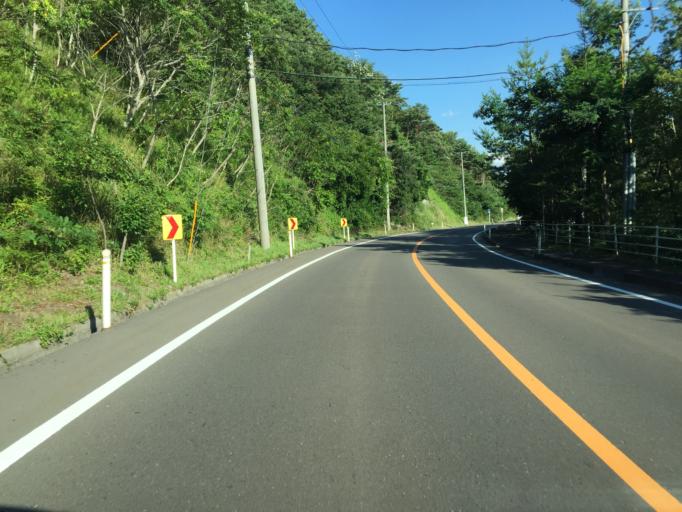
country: JP
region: Miyagi
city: Shiroishi
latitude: 37.9765
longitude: 140.4972
